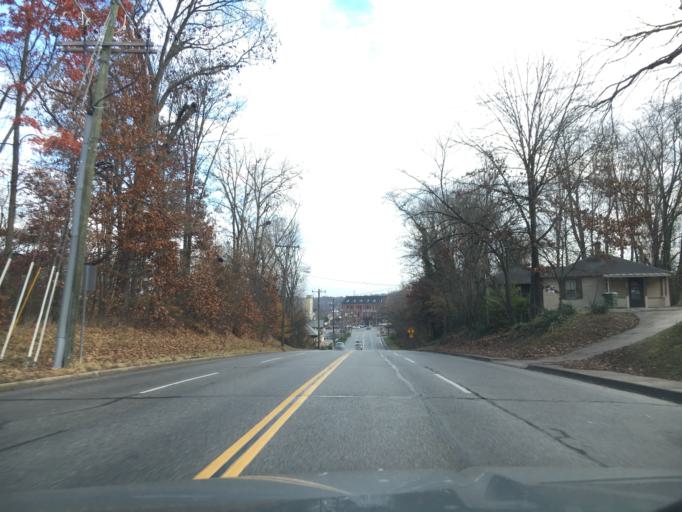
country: US
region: Virginia
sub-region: Prince Edward County
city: Farmville
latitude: 37.3044
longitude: -78.3997
